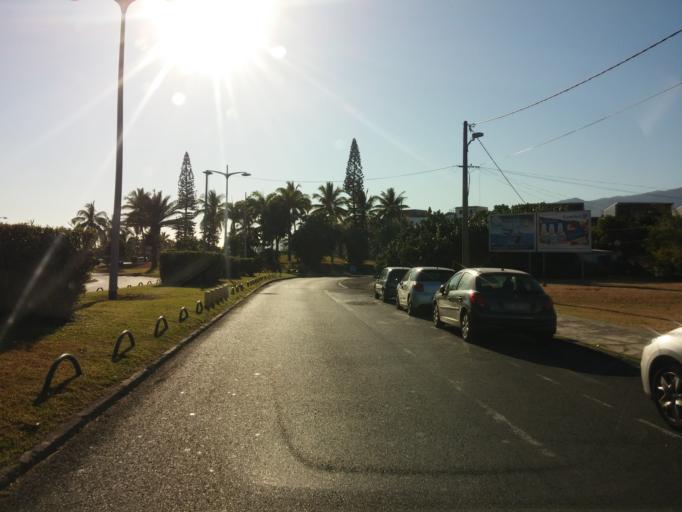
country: RE
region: Reunion
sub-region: Reunion
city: Le Port
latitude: -20.9319
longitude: 55.2962
